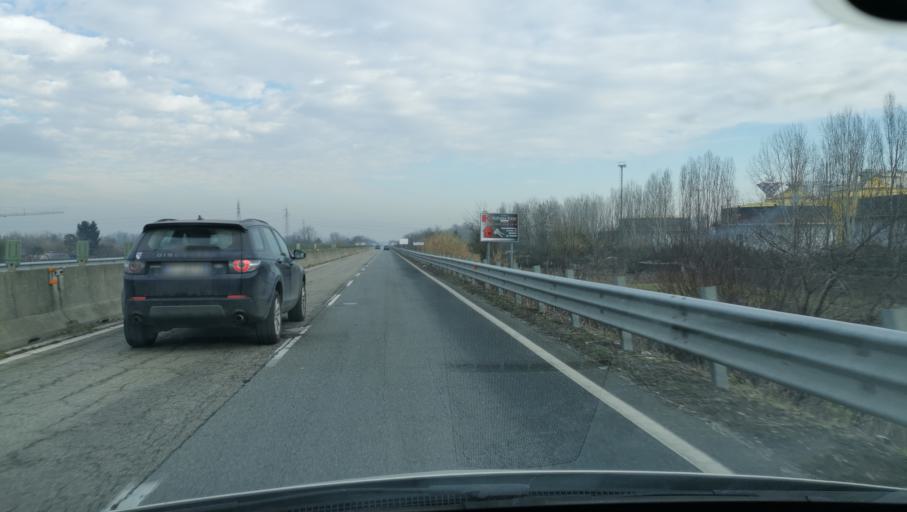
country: IT
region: Piedmont
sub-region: Provincia di Torino
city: Castiglione Torinese
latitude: 45.1350
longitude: 7.7886
